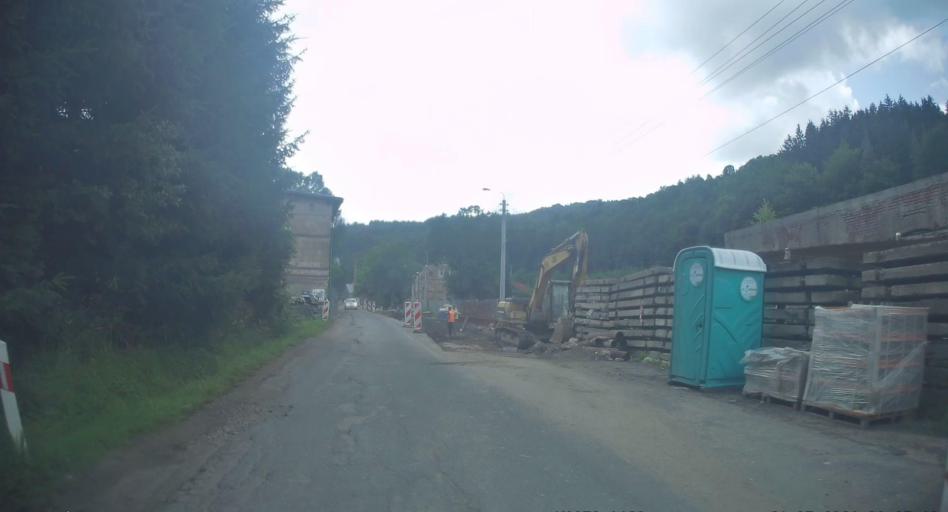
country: PL
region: Lower Silesian Voivodeship
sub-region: Powiat walbrzyski
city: Walim
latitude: 50.7205
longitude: 16.4165
